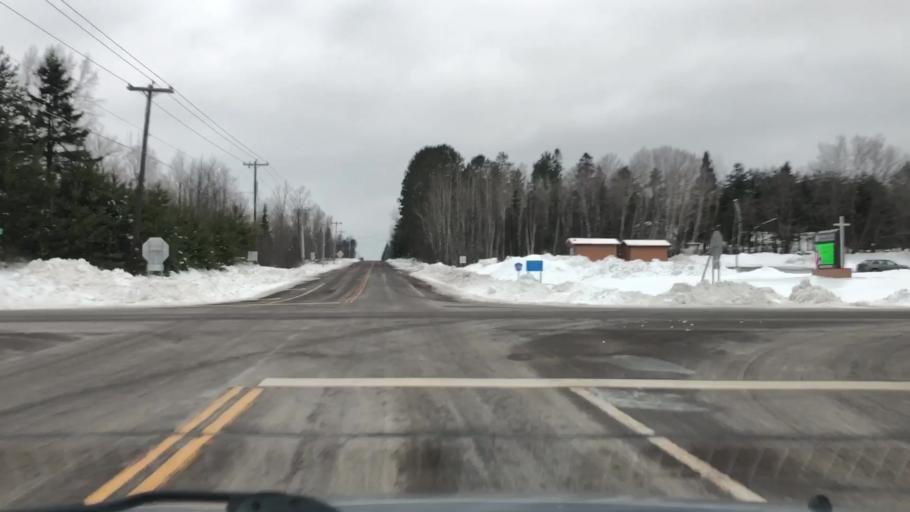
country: US
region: Minnesota
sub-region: Saint Louis County
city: Arnold
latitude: 46.8653
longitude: -92.1111
